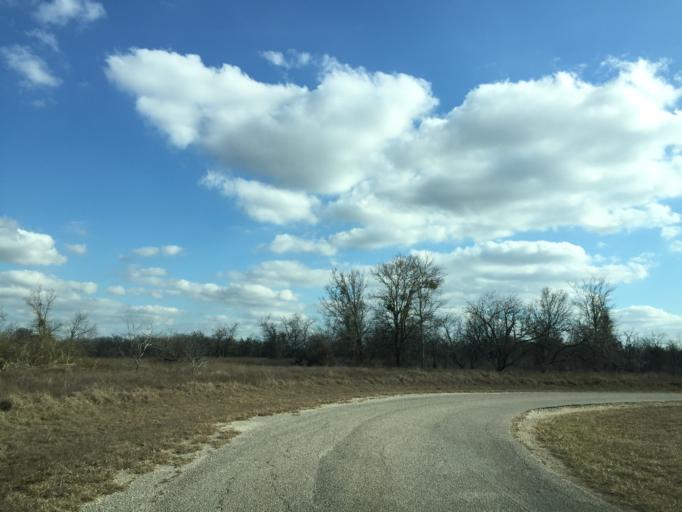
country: US
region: Texas
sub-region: Williamson County
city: Granger
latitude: 30.6750
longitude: -97.3623
